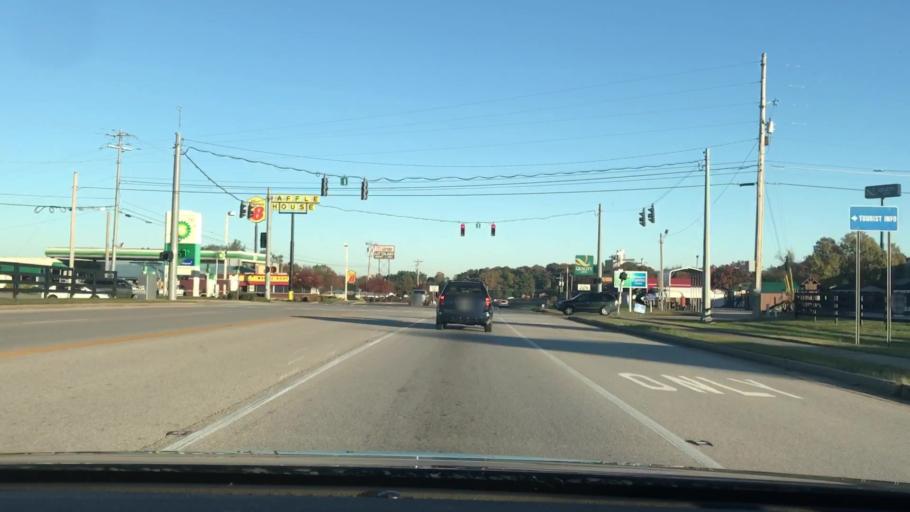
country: US
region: Kentucky
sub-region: Simpson County
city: Franklin
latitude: 36.6685
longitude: -86.5576
